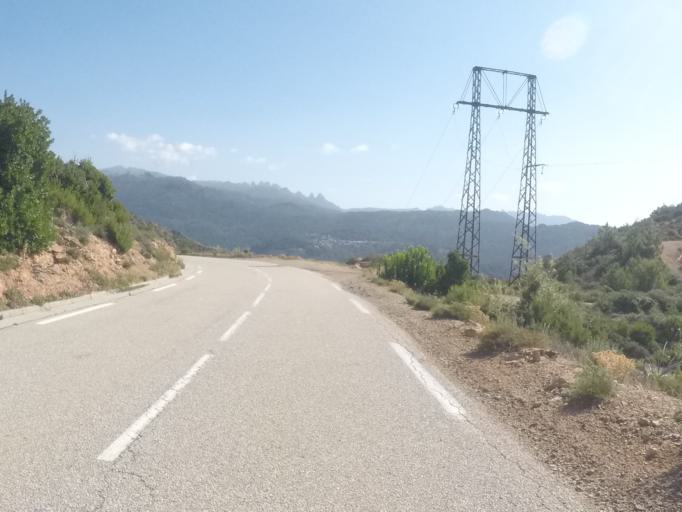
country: FR
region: Corsica
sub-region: Departement de la Corse-du-Sud
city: Olmeto
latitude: 41.7645
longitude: 9.0406
